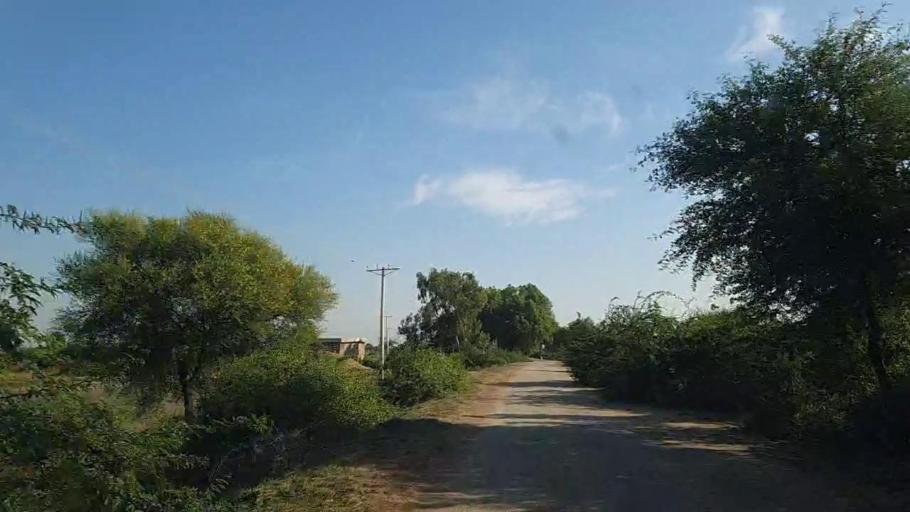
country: PK
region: Sindh
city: Bulri
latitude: 24.7821
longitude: 68.3528
